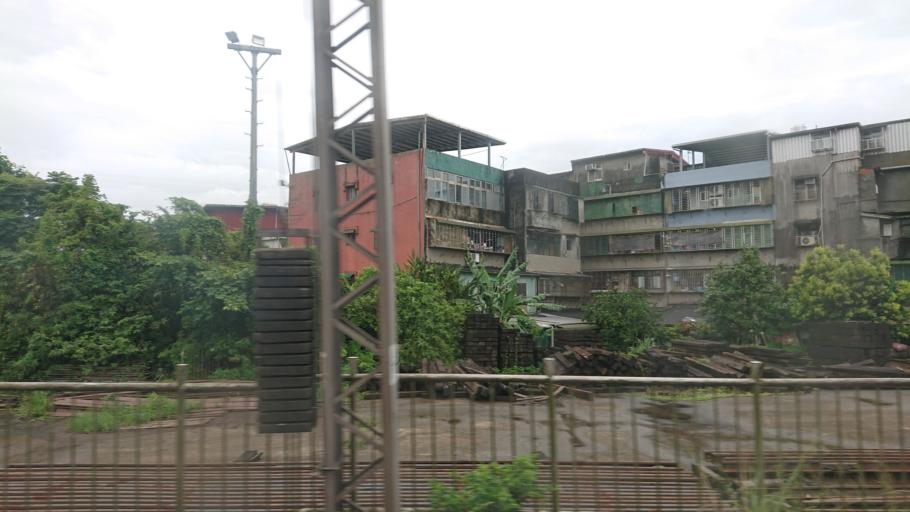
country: TW
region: Taiwan
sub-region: Keelung
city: Keelung
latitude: 25.0961
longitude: 121.7183
